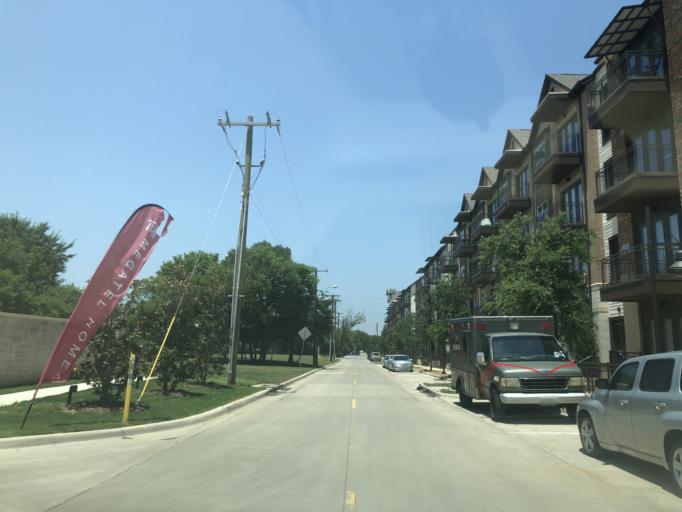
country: US
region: Texas
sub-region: Dallas County
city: Dallas
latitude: 32.7765
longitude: -96.8421
